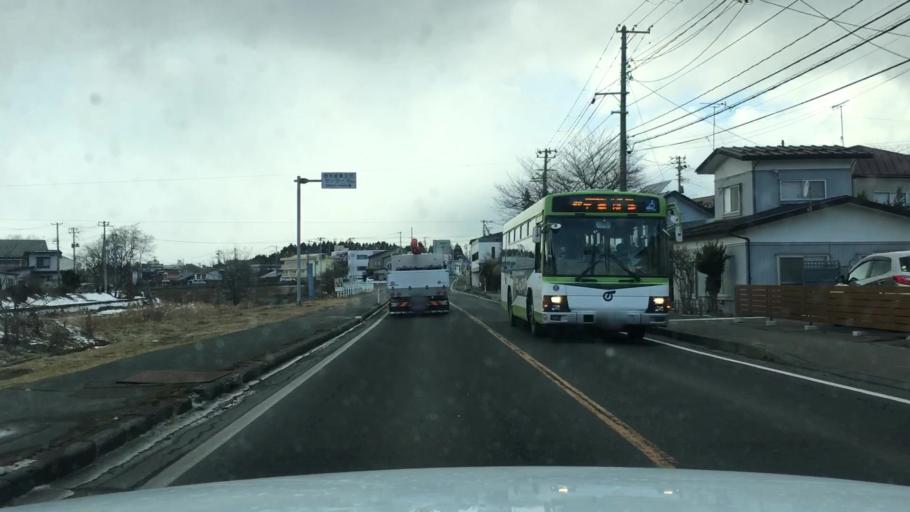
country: JP
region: Iwate
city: Morioka-shi
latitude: 39.6901
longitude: 141.1752
